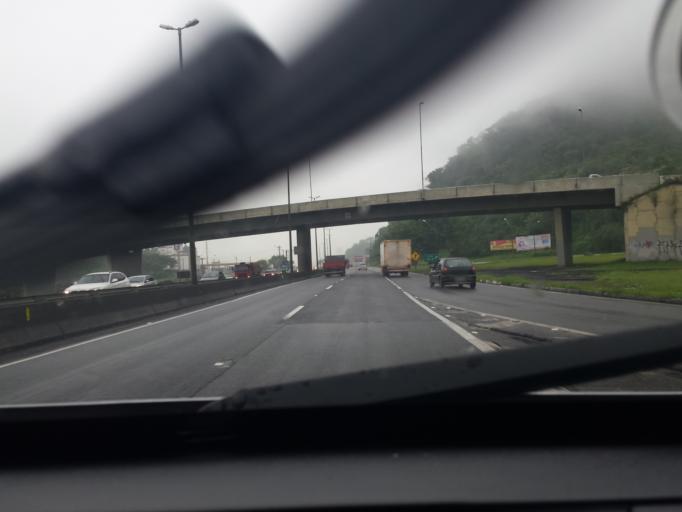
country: BR
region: Santa Catarina
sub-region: Navegantes
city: Navegantes
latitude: -26.8422
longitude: -48.7167
